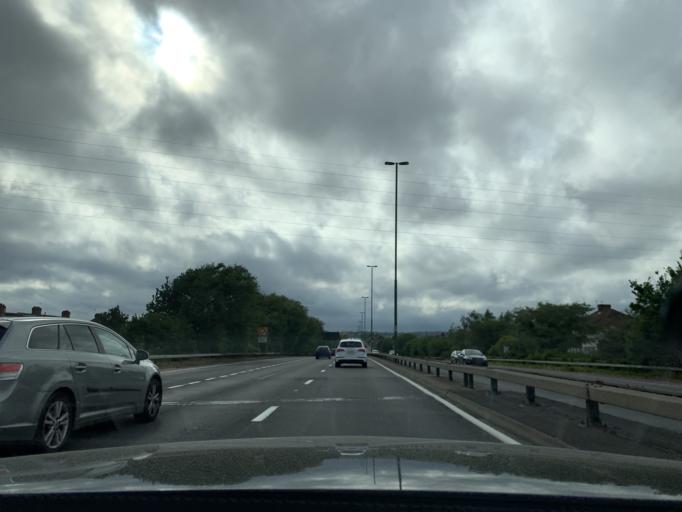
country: GB
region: England
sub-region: Greater London
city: Welling
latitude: 51.4520
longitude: 0.1038
